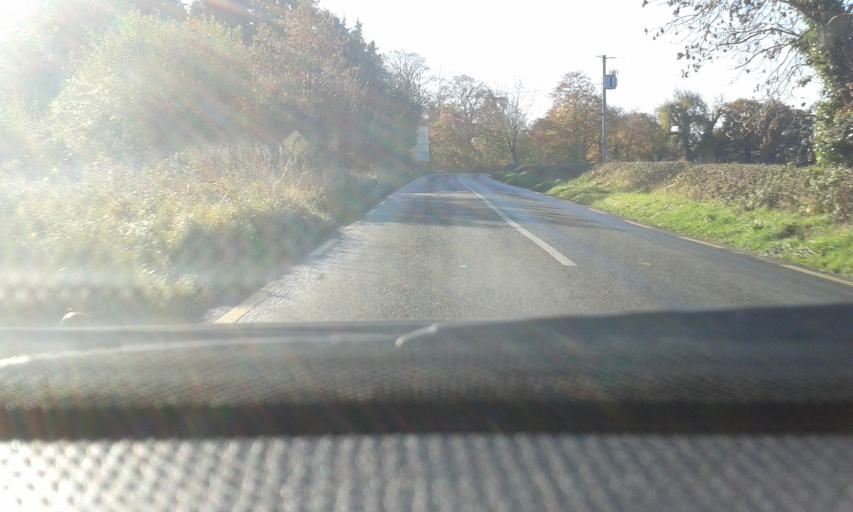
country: IE
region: Leinster
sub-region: Kildare
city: Monasterevin
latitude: 53.1589
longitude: -7.0408
